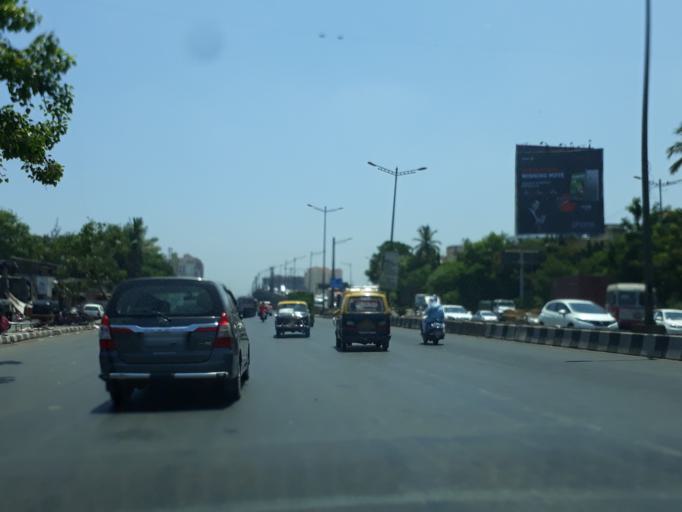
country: IN
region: Maharashtra
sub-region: Mumbai Suburban
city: Mumbai
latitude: 19.0688
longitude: 72.9040
